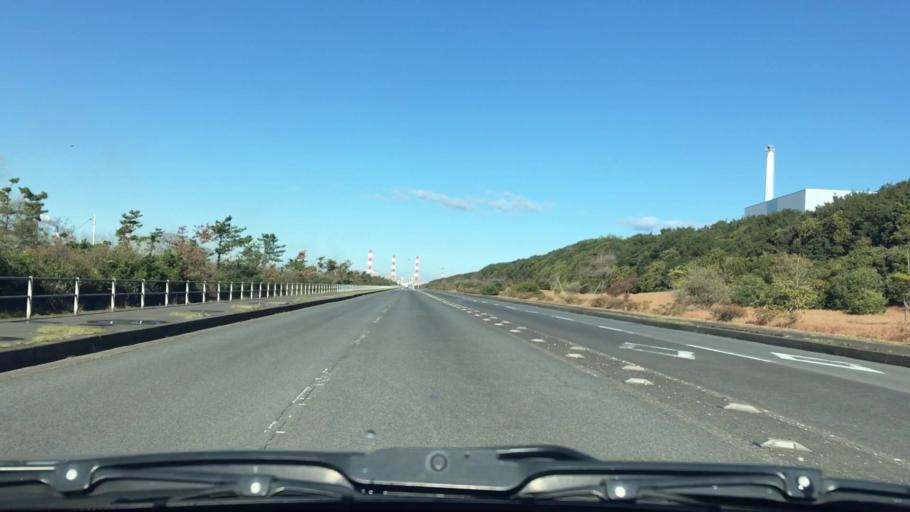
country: JP
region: Chiba
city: Omigawa
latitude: 35.8739
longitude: 140.7345
